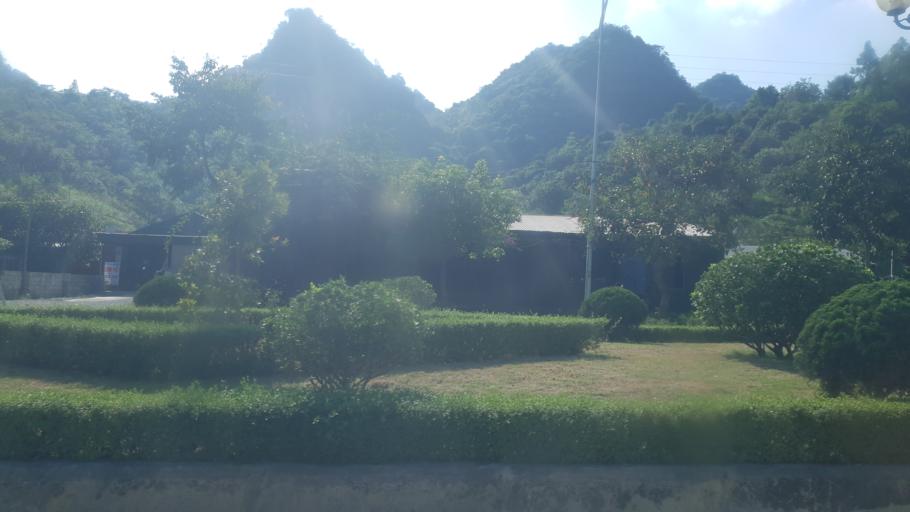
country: VN
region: Lang Son
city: Thi Tran Cao Loc
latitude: 21.9603
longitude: 106.7061
